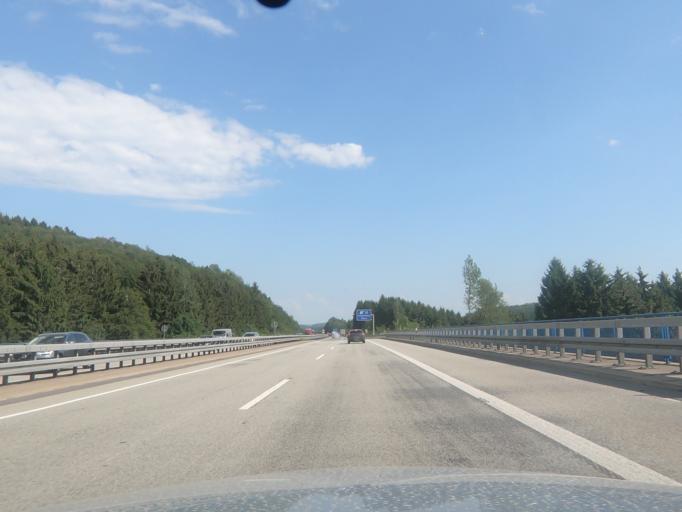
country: DE
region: North Rhine-Westphalia
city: Freudenberg
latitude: 50.9192
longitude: 7.9003
